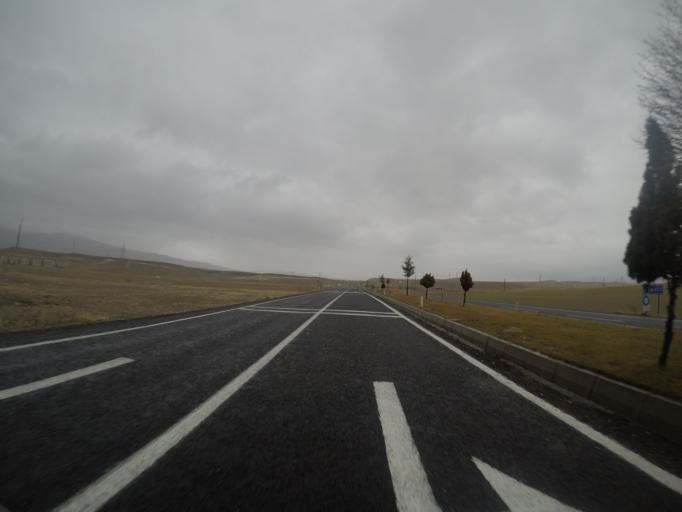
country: TR
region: Nevsehir
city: Avanos
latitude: 38.7013
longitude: 34.8674
